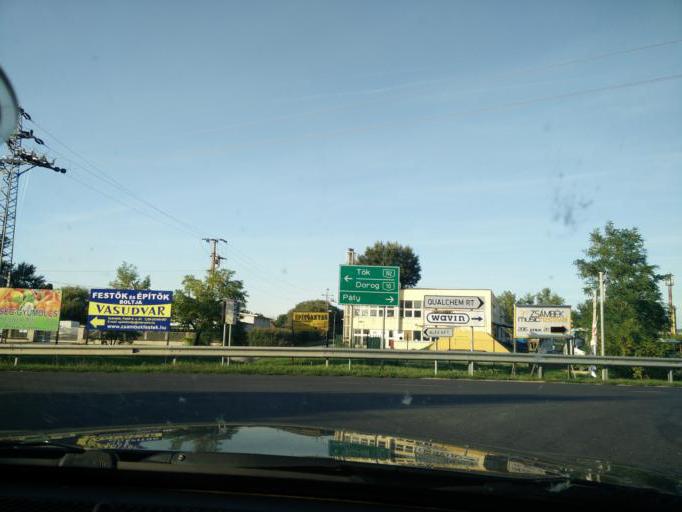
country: HU
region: Pest
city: Zsambek
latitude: 47.5448
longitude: 18.7272
